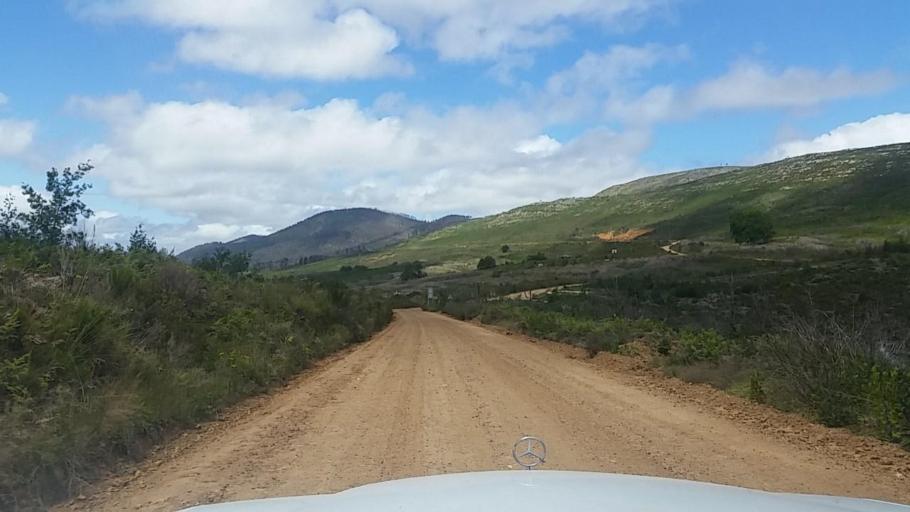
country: ZA
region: Western Cape
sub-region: Eden District Municipality
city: Knysna
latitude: -33.8814
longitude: 23.1567
